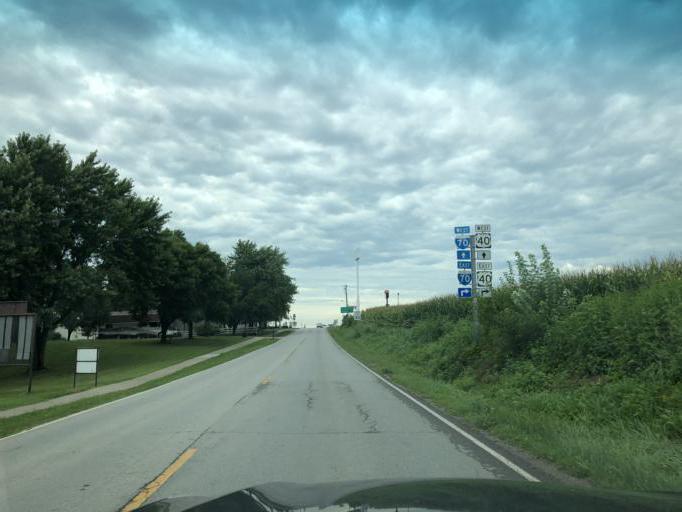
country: US
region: Missouri
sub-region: Saline County
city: Sweet Springs
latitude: 38.9741
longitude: -93.4151
